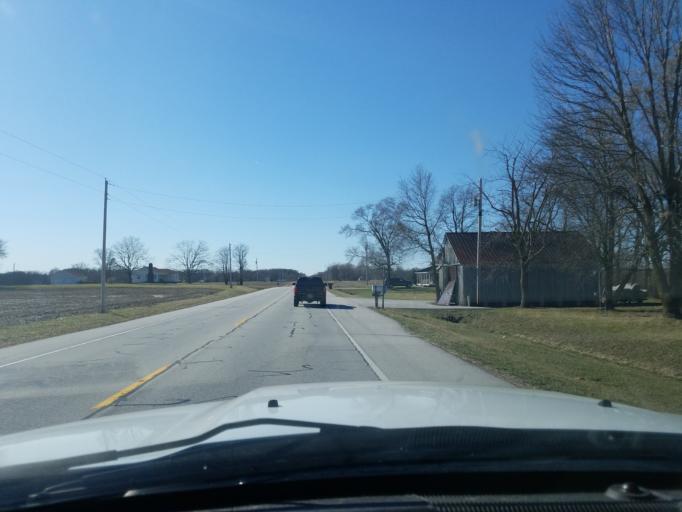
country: US
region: Indiana
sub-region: Johnson County
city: Franklin
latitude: 39.4952
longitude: -85.9370
